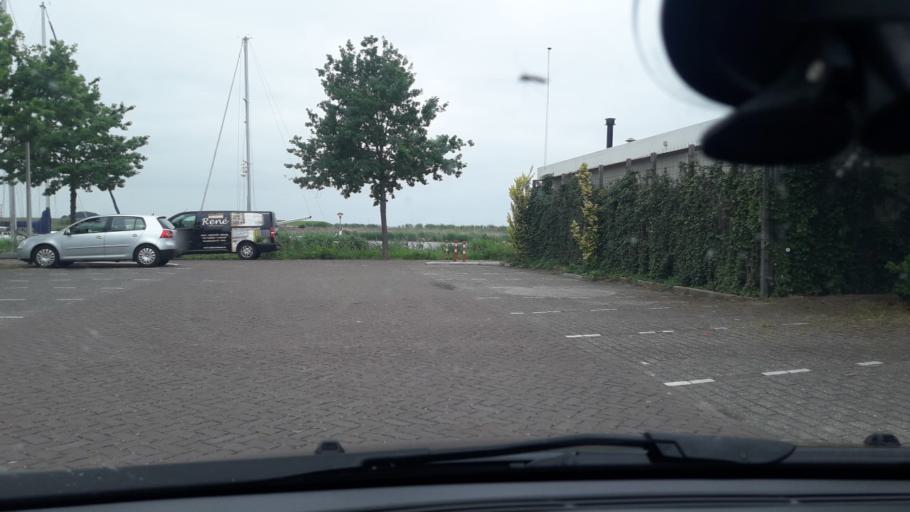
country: NL
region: Flevoland
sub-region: Gemeente Dronten
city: Dronten
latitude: 52.5808
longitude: 5.7611
